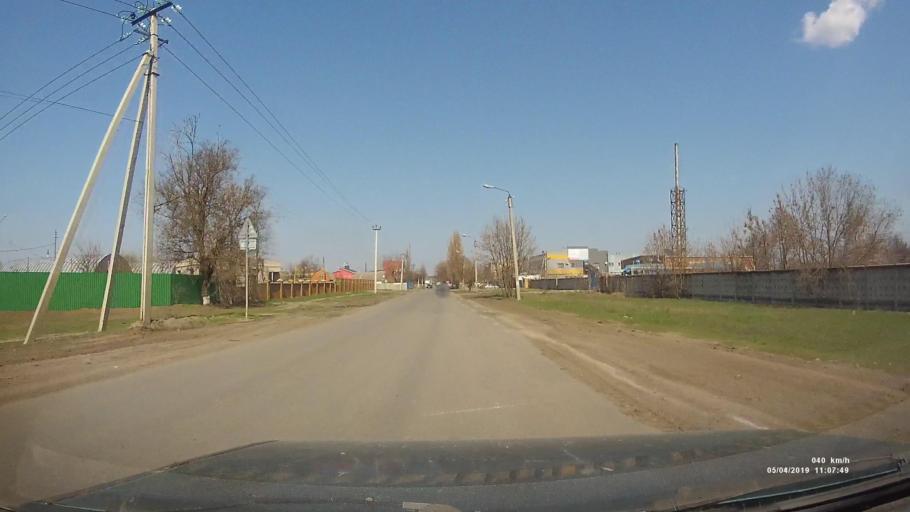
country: RU
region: Rostov
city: Azov
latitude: 47.0828
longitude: 39.4372
